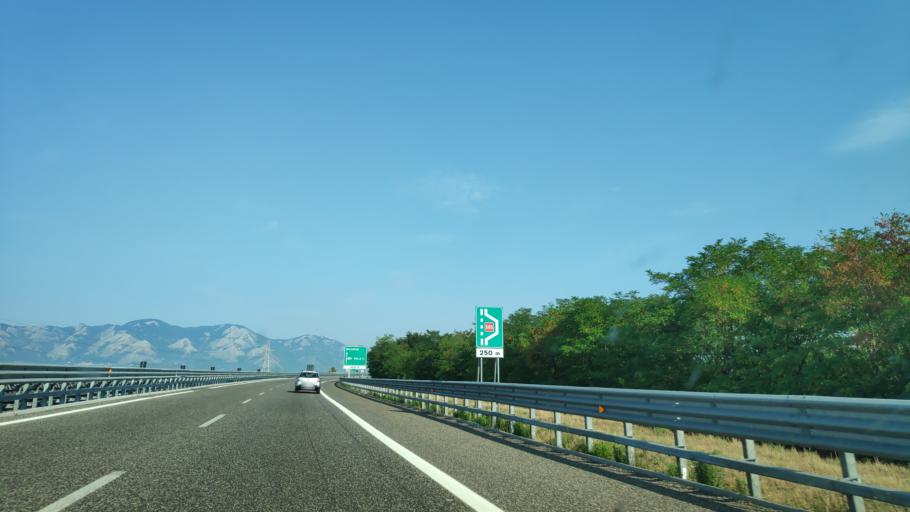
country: IT
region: Campania
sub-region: Provincia di Salerno
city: Sala Consilina
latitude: 40.4091
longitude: 15.5669
